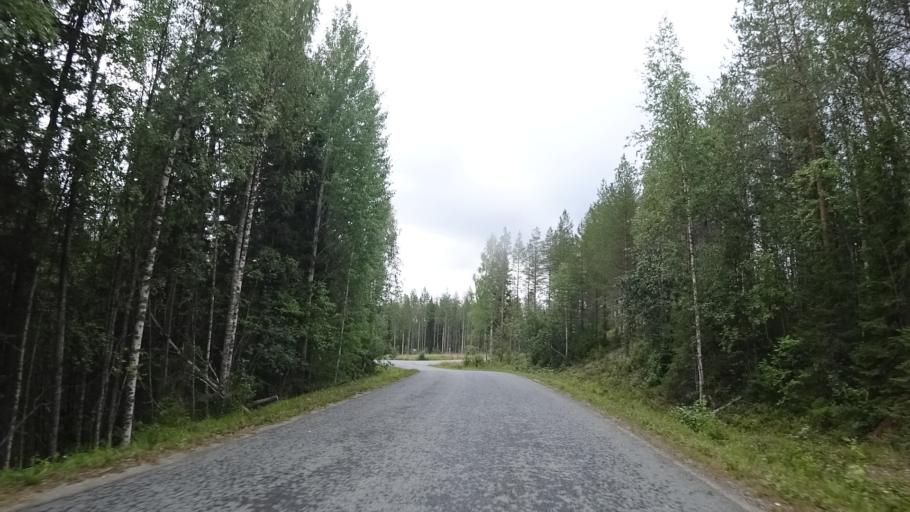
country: FI
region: North Karelia
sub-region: Joensuu
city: Ilomantsi
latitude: 62.9797
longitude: 31.2814
